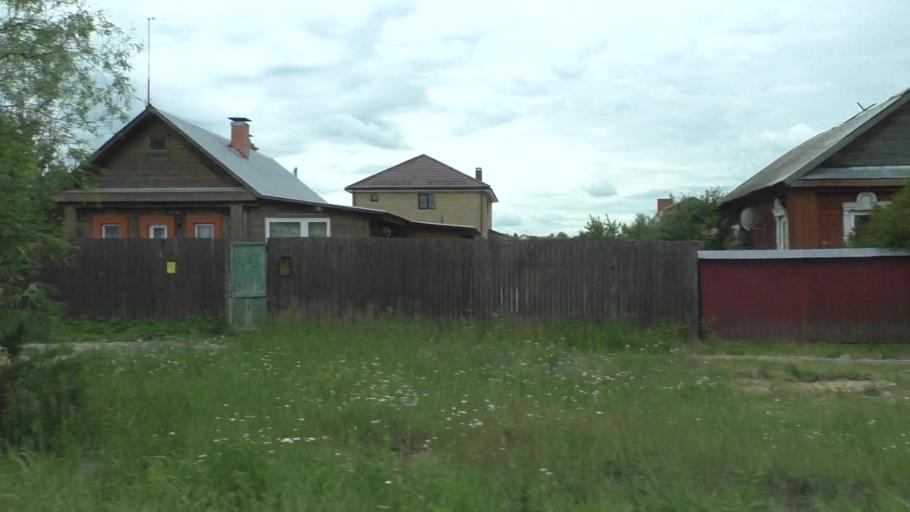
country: RU
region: Moskovskaya
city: Il'inskiy Pogost
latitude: 55.5019
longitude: 38.7962
